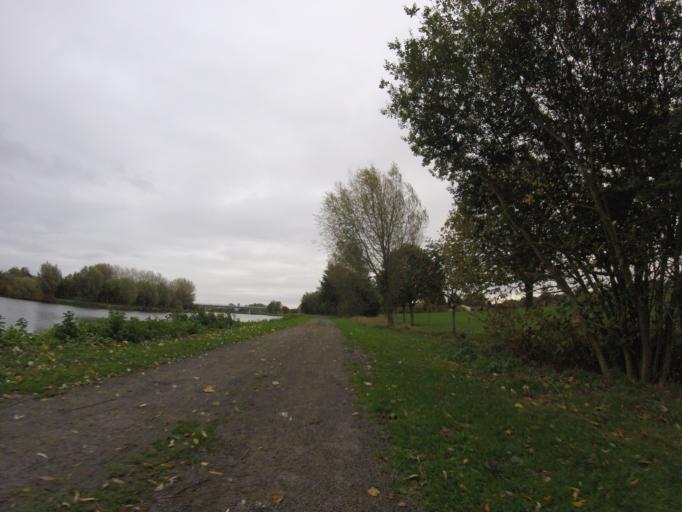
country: FR
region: Nord-Pas-de-Calais
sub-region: Departement du Nord
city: Quesnoy-sur-Deule
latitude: 50.6989
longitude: 3.0193
